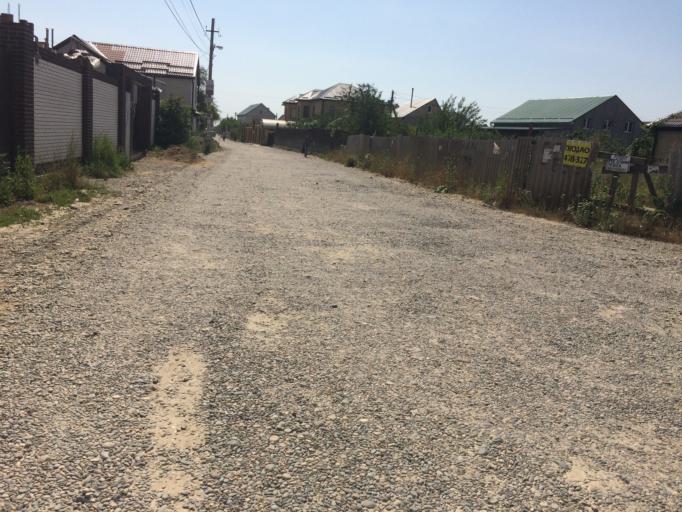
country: RU
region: Stavropol'skiy
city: Tatarka
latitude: 44.9884
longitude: 41.9376
